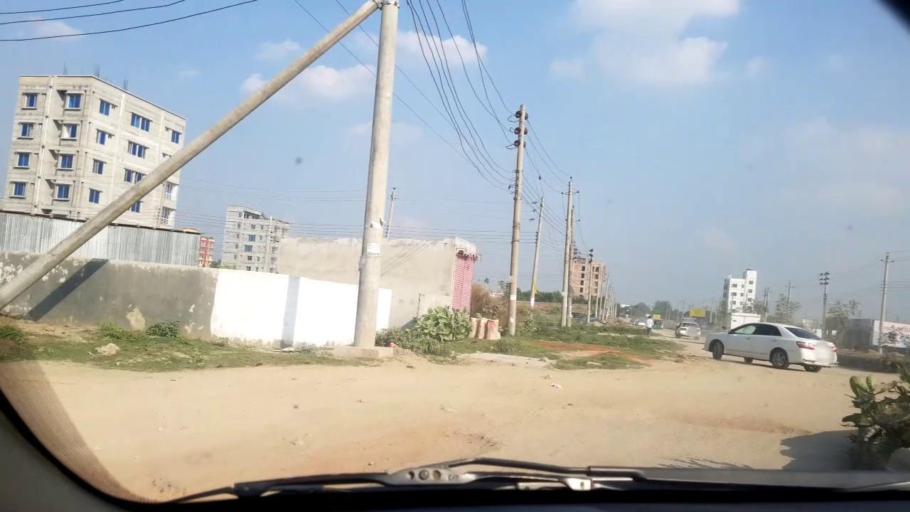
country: BD
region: Dhaka
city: Tungi
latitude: 23.8676
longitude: 90.3706
